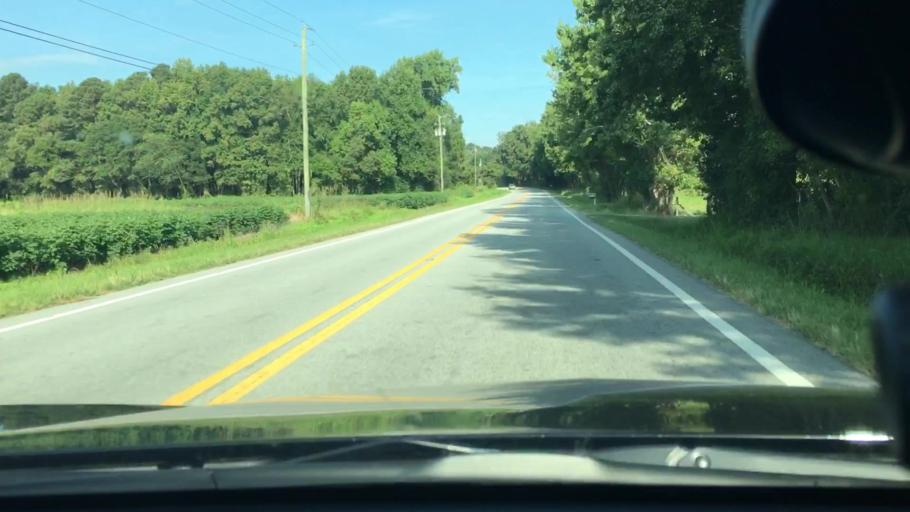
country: US
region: North Carolina
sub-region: Pitt County
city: Farmville
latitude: 35.6945
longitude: -77.5009
